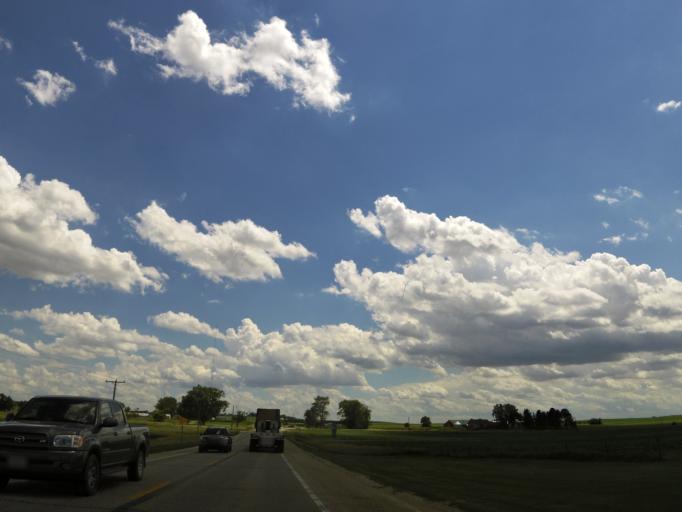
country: US
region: Iowa
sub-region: Benton County
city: Urbana
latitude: 42.3158
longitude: -91.8895
